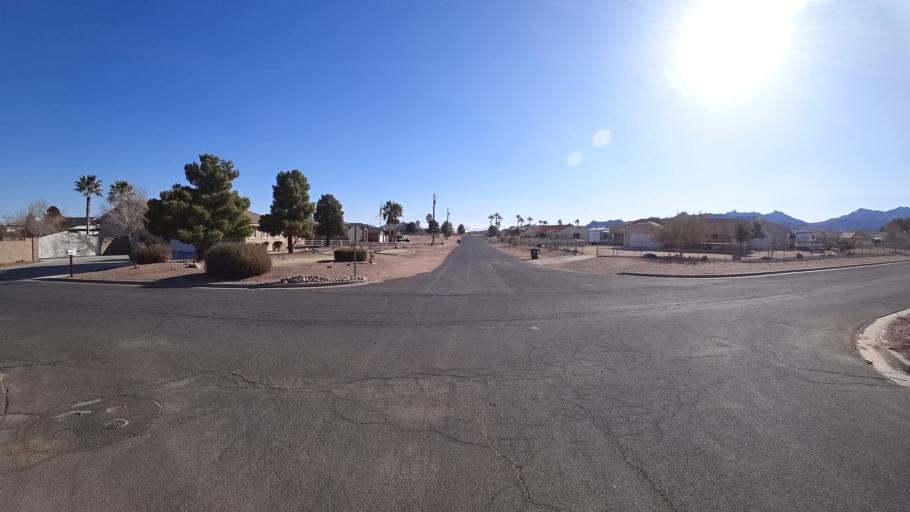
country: US
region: Arizona
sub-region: Mohave County
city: Kingman
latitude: 35.2065
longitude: -113.9986
